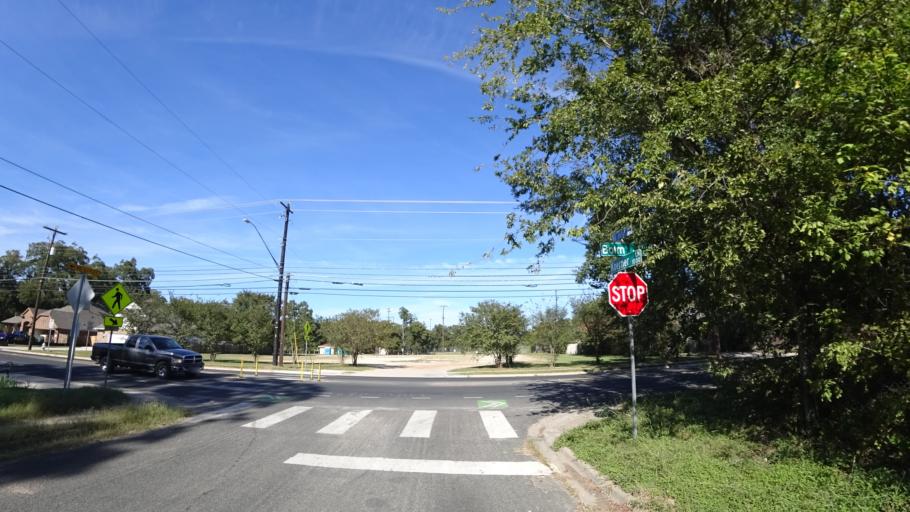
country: US
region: Texas
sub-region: Travis County
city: Austin
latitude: 30.2580
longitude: -97.6903
